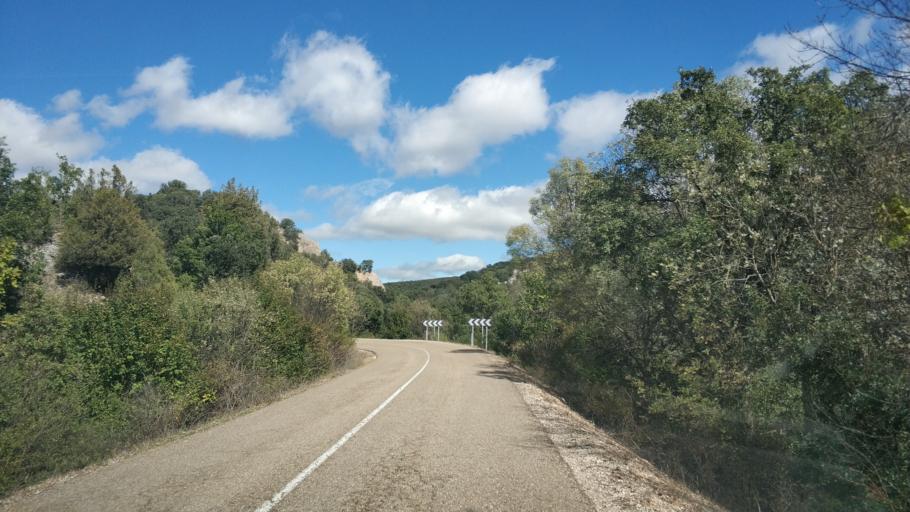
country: ES
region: Castille and Leon
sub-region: Provincia de Burgos
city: Retuerta
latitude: 42.0433
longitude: -3.4702
